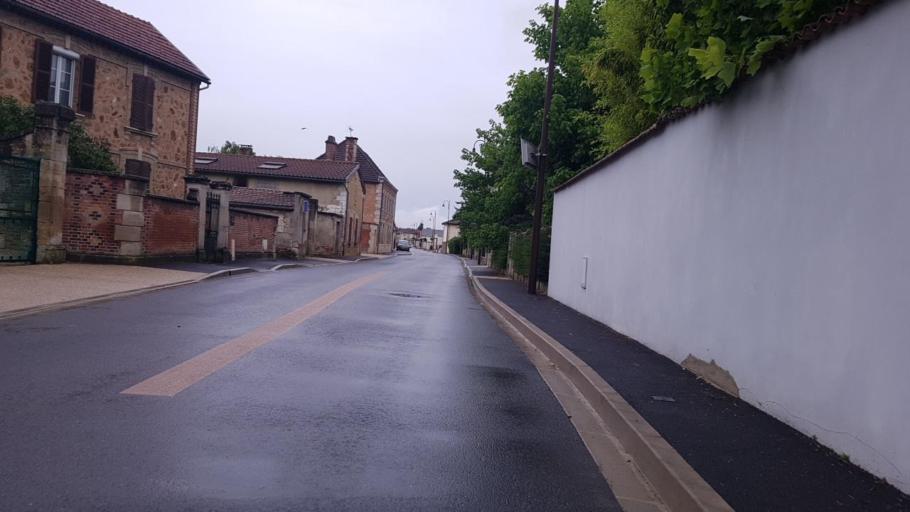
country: FR
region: Champagne-Ardenne
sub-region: Departement de la Marne
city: Sarry
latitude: 48.9167
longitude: 4.4106
